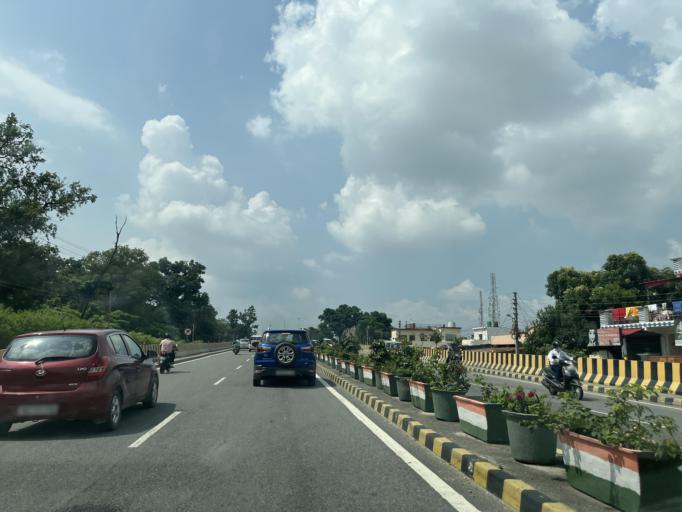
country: IN
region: Uttarakhand
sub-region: Dehradun
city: Raipur
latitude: 30.2739
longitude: 78.0770
